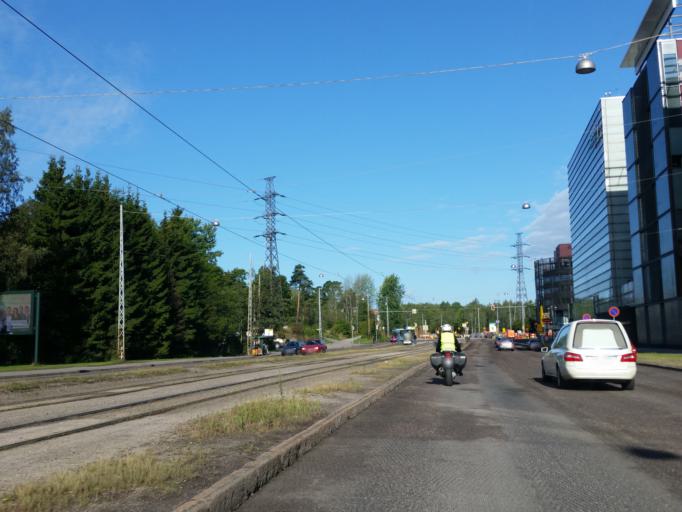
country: FI
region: Uusimaa
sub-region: Helsinki
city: Helsinki
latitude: 60.1938
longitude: 24.8934
